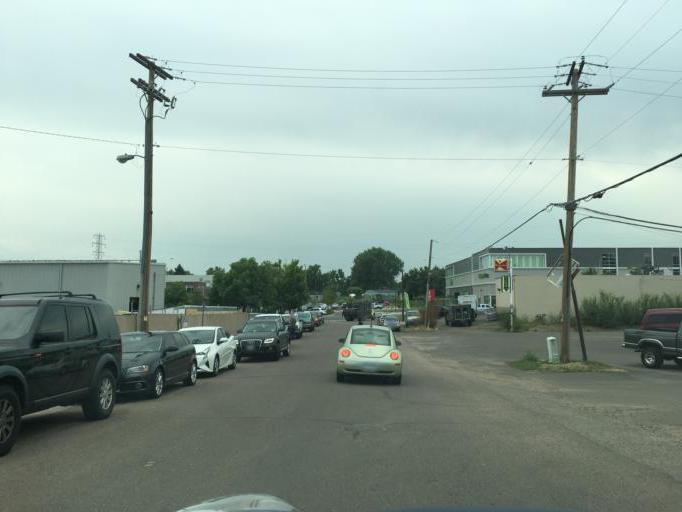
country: US
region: Colorado
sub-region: Jefferson County
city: Wheat Ridge
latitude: 39.7413
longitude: -105.1014
